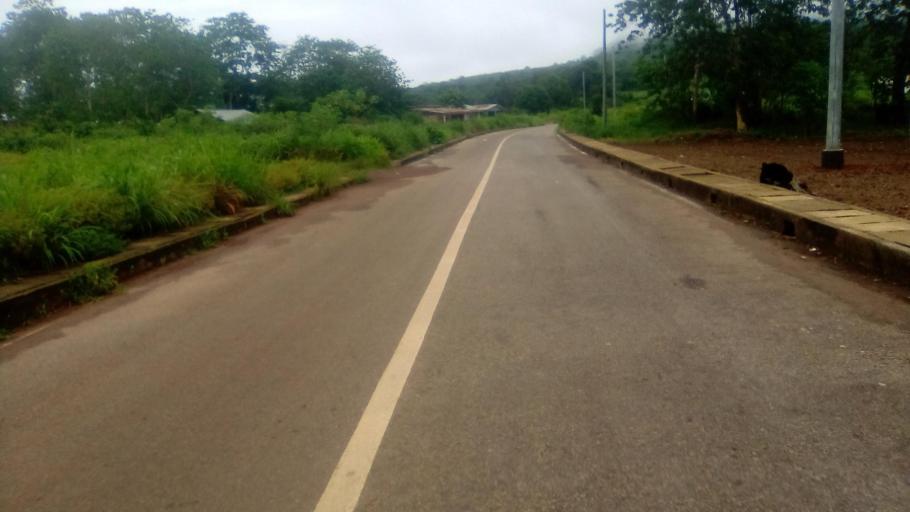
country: SL
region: Southern Province
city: Moyamba
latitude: 8.1621
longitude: -12.4479
